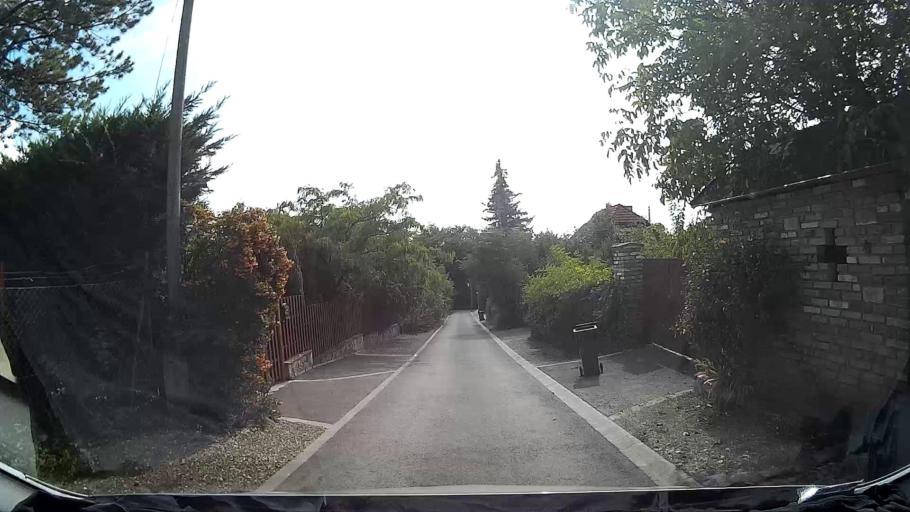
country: HU
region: Pest
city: Szentendre
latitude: 47.6838
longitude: 19.0691
